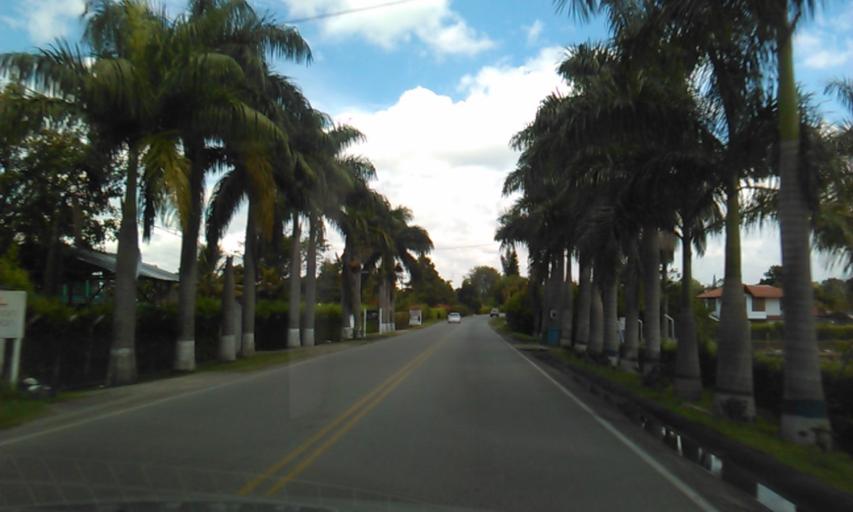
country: CO
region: Quindio
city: Armenia
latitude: 4.4747
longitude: -75.7025
